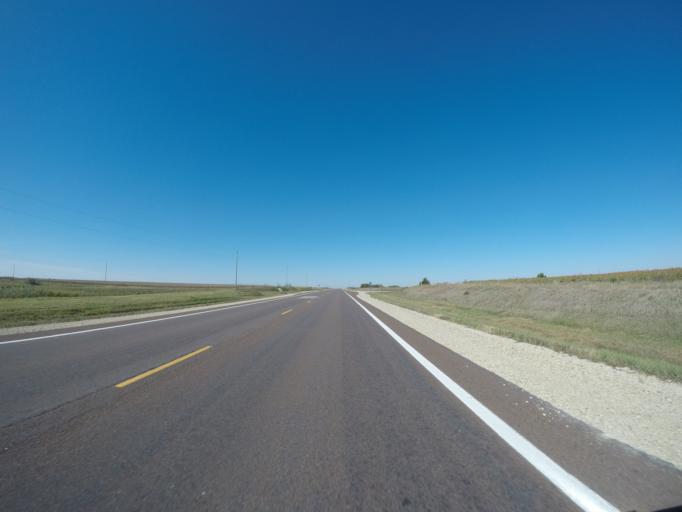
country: US
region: Kansas
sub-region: Riley County
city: Fort Riley North
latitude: 39.3064
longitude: -96.8670
